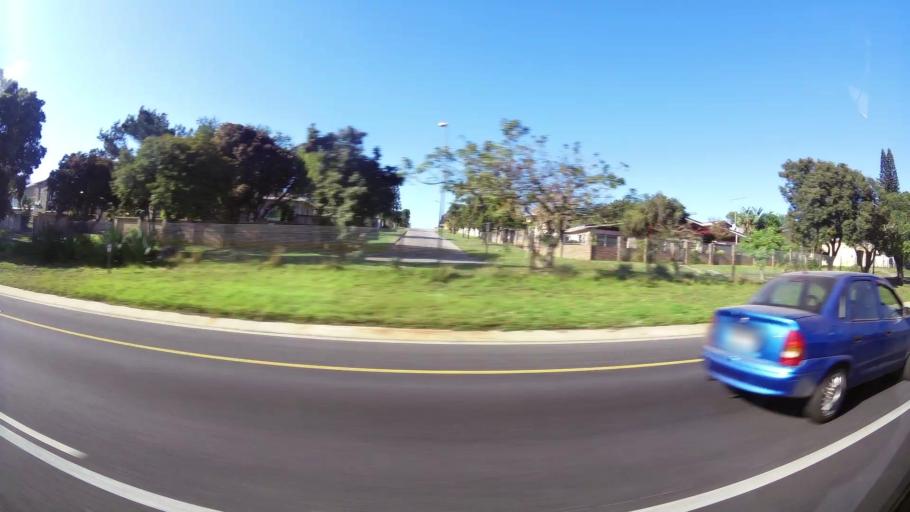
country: ZA
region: Eastern Cape
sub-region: Nelson Mandela Bay Metropolitan Municipality
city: Port Elizabeth
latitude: -33.9371
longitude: 25.5546
